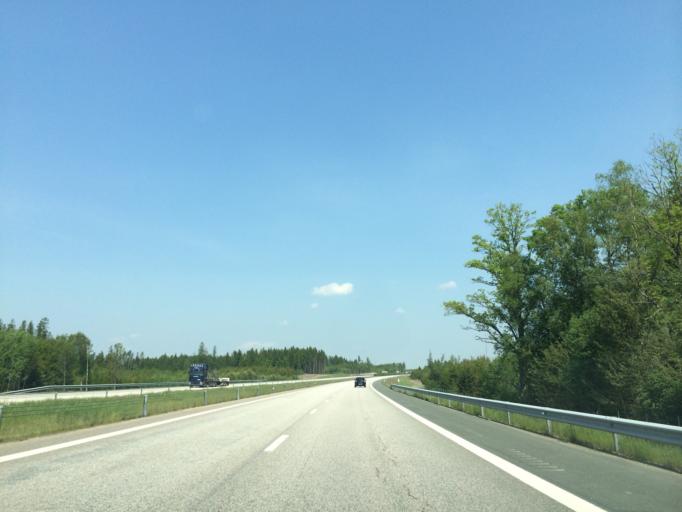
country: SE
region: Joenkoeping
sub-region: Varnamo Kommun
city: Bor
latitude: 57.0770
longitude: 14.0627
